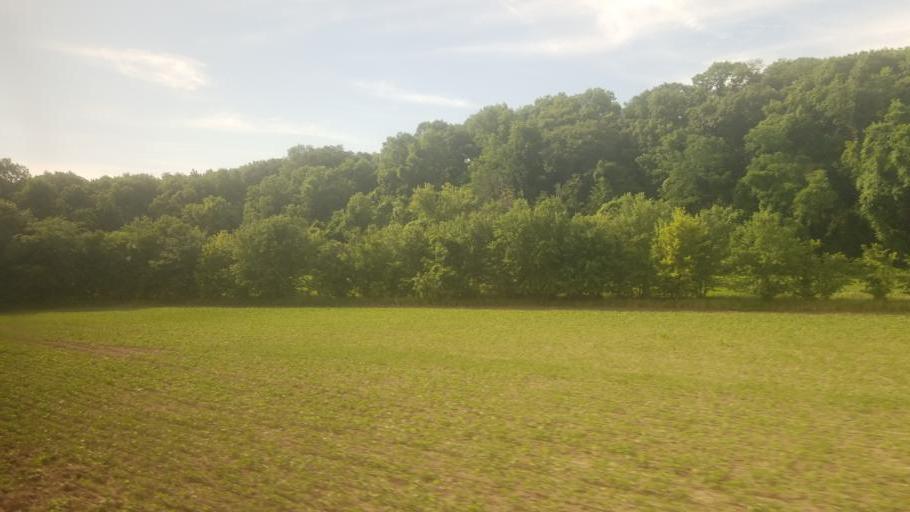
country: US
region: Kansas
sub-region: Johnson County
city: De Soto
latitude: 38.9809
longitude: -94.9900
